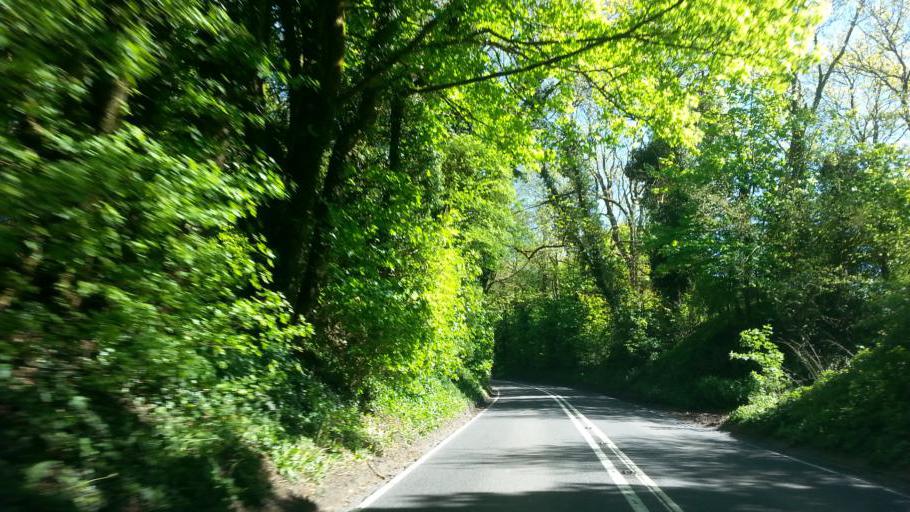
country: GB
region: England
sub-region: Dorset
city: Shaftesbury
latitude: 51.0268
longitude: -2.1900
